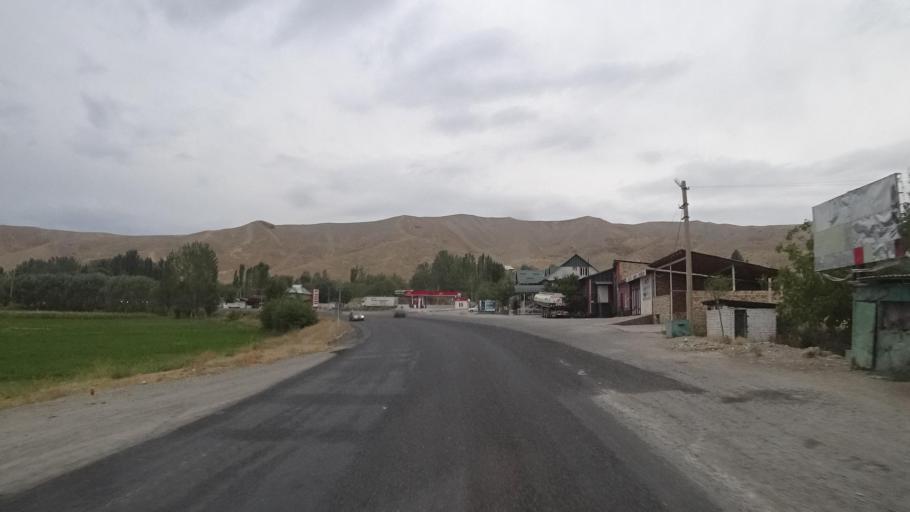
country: UZ
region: Namangan
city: Uchqurghon Shahri
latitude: 41.0843
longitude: 72.3519
